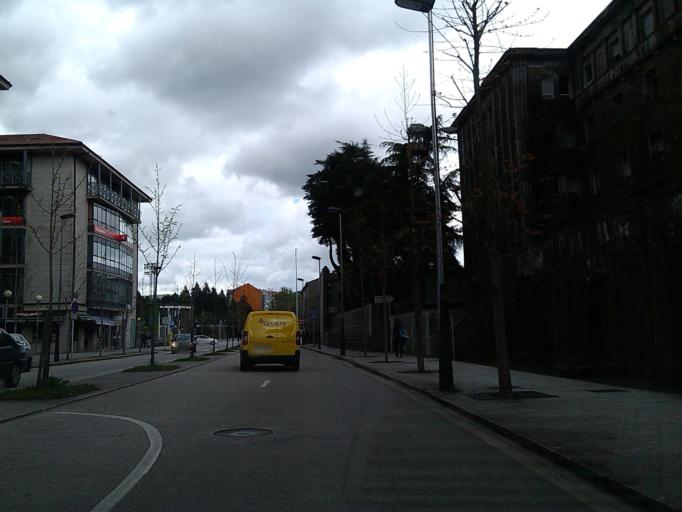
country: ES
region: Galicia
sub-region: Provincia da Coruna
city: Santiago de Compostela
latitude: 42.8835
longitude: -8.5484
